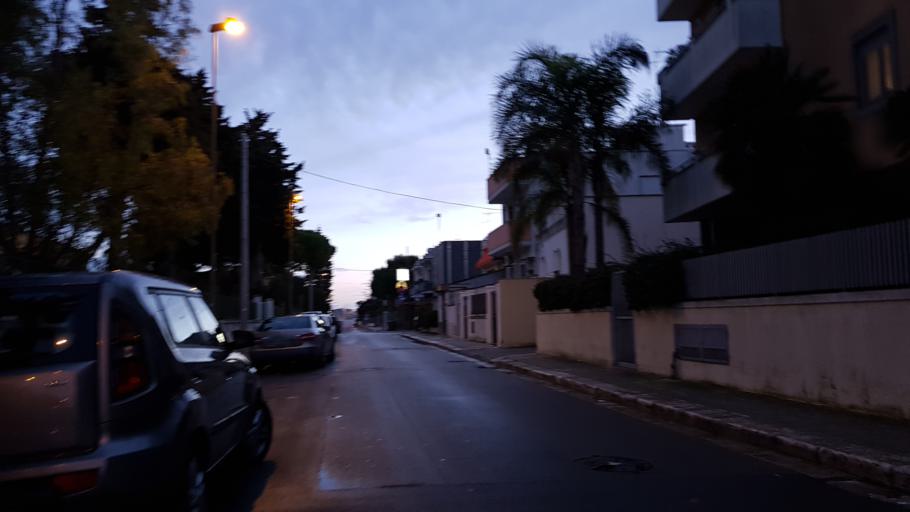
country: IT
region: Apulia
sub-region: Provincia di Brindisi
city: Materdomini
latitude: 40.6476
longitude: 17.9441
